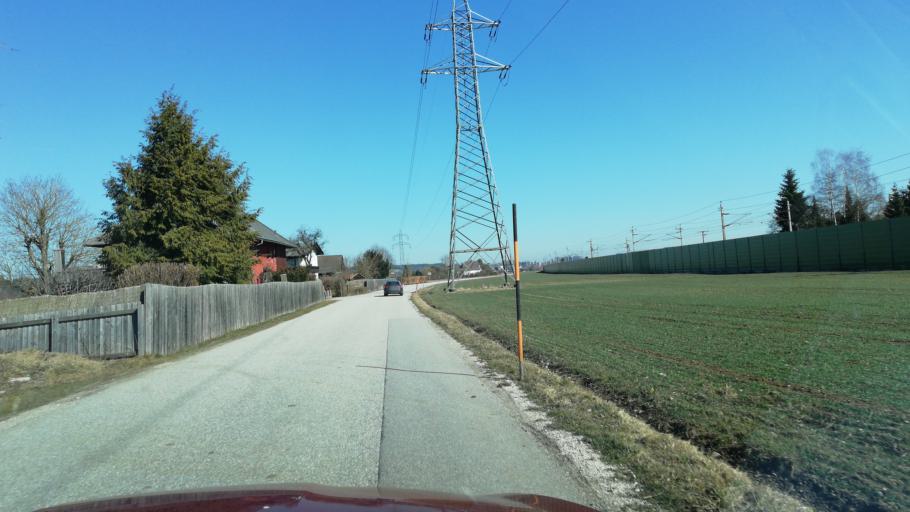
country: AT
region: Upper Austria
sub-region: Politischer Bezirk Vocklabruck
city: Oberndorf bei Schwanenstadt
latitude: 48.0383
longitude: 13.7445
